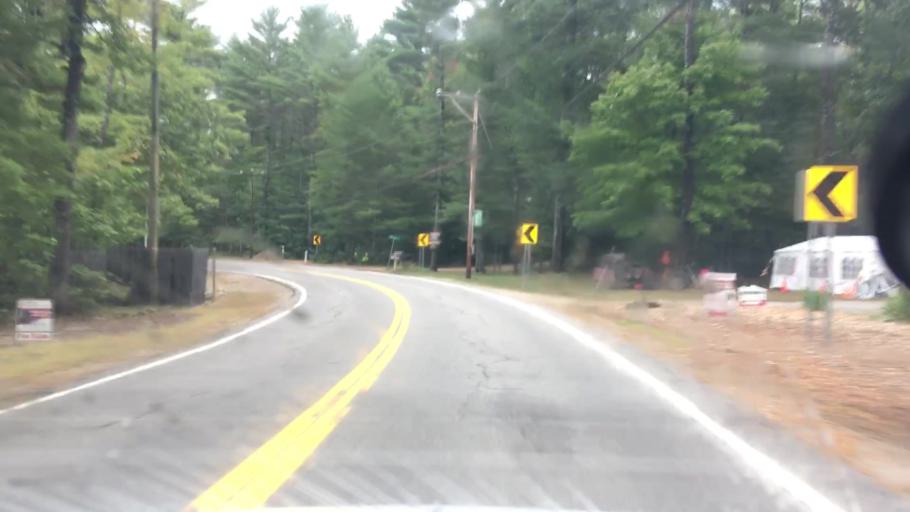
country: US
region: New Hampshire
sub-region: Carroll County
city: Wakefield
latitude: 43.6277
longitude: -70.9851
